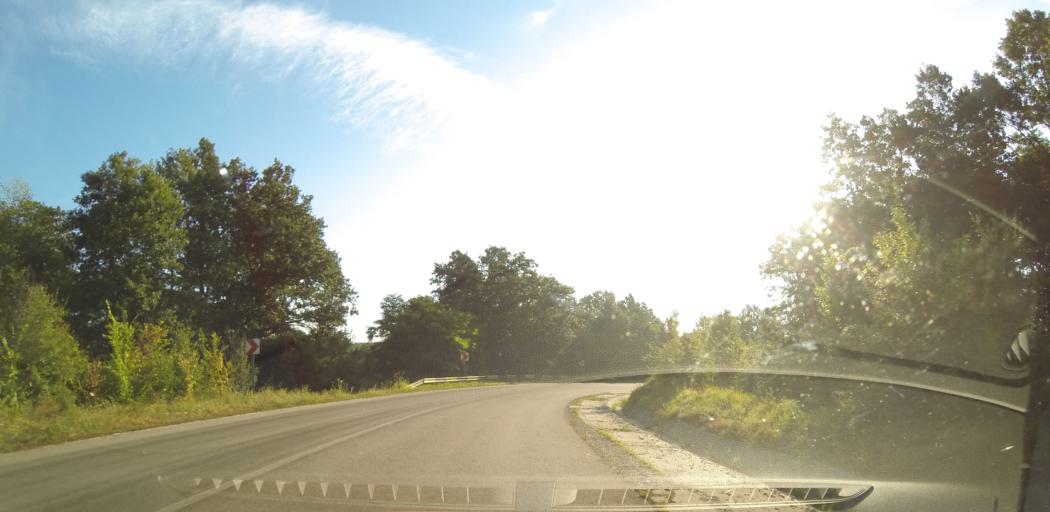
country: RO
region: Valcea
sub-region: Comuna Balcesti
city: Balcesti
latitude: 44.5912
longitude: 23.9157
